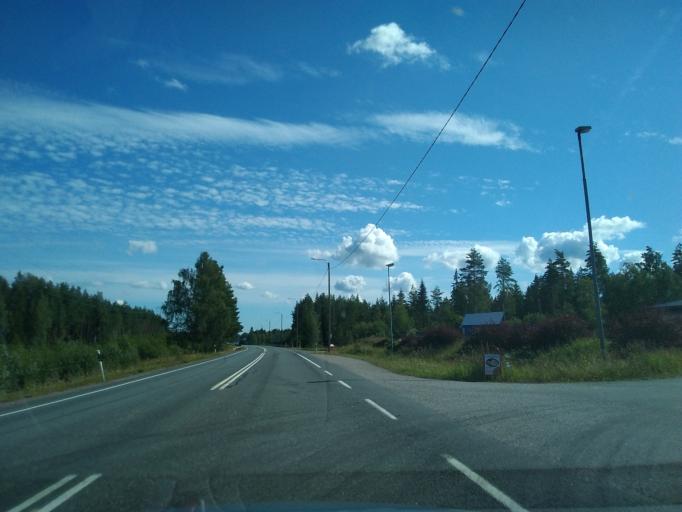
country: FI
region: Haeme
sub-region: Haemeenlinna
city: Haemeenlinna
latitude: 60.9605
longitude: 24.4380
